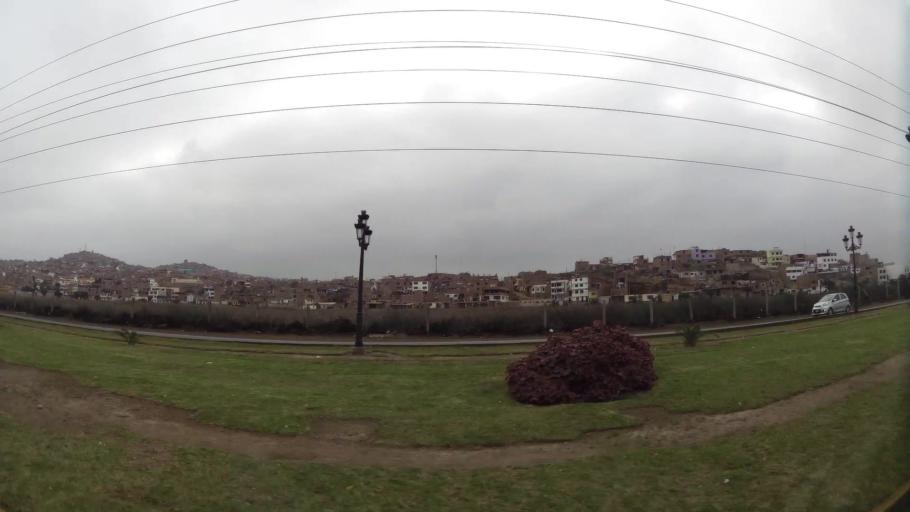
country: PE
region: Lima
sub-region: Lima
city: Surco
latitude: -12.2041
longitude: -76.9928
